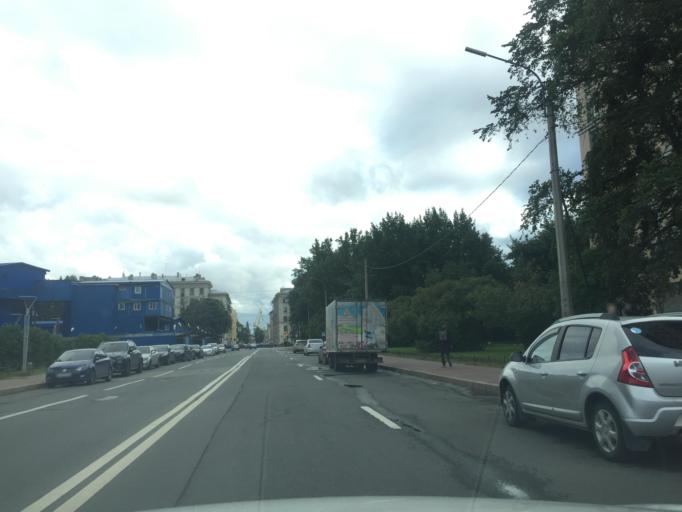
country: RU
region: St.-Petersburg
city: Vasyl'evsky Ostrov
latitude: 59.9329
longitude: 30.2549
